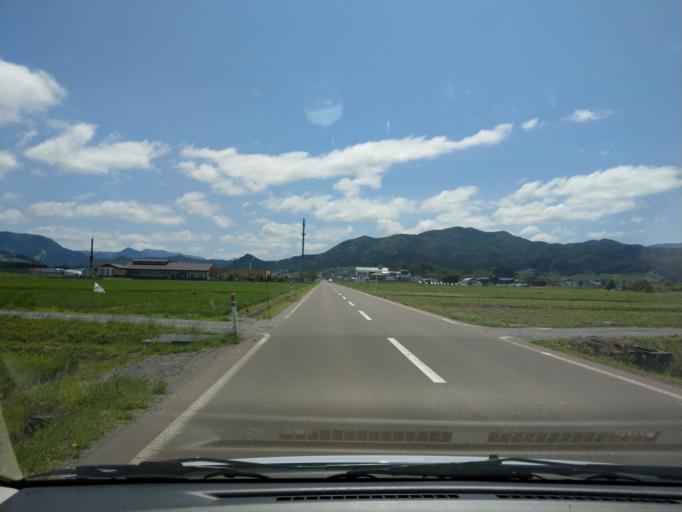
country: JP
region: Aomori
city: Hirosaki
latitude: 40.5584
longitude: 140.5506
